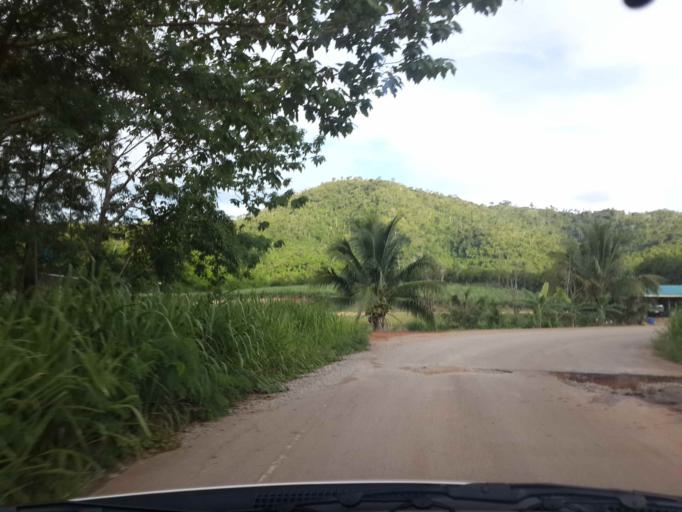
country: TH
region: Kanchanaburi
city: Dan Makham Tia
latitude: 13.7456
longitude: 99.1988
